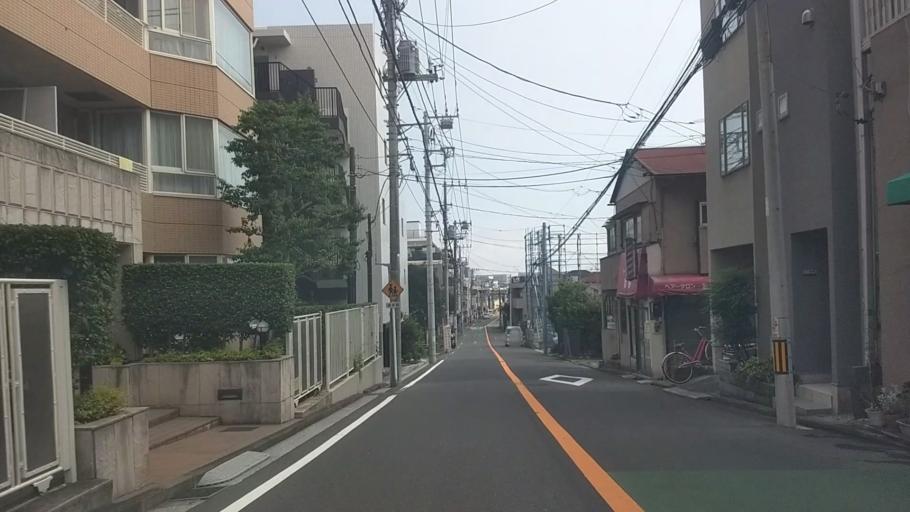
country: JP
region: Kanagawa
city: Yokohama
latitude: 35.4943
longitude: 139.6385
